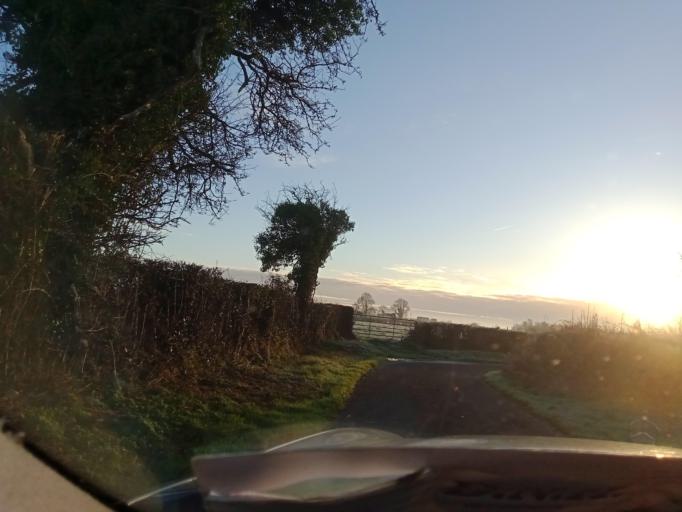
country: IE
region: Leinster
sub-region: Kilkenny
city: Callan
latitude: 52.5419
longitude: -7.4242
